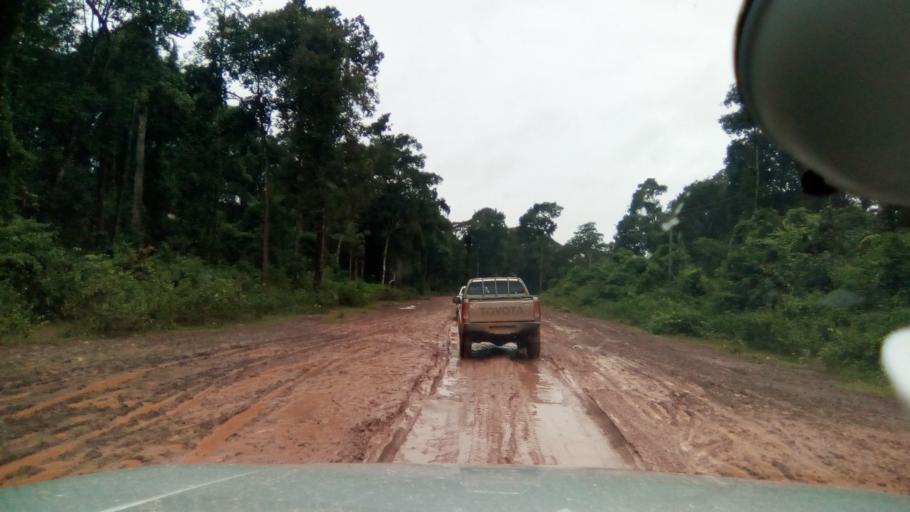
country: LA
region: Attapu
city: Attapu
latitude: 14.6837
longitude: 106.5540
